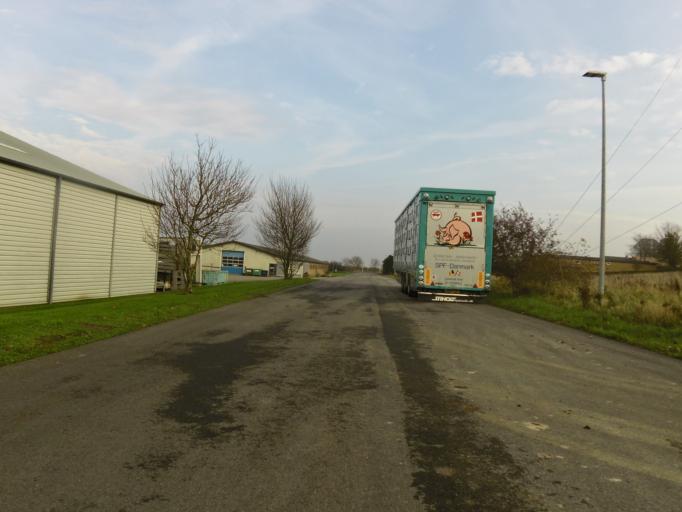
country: DK
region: South Denmark
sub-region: Sonderborg Kommune
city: Dybbol
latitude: 54.9241
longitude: 9.7356
